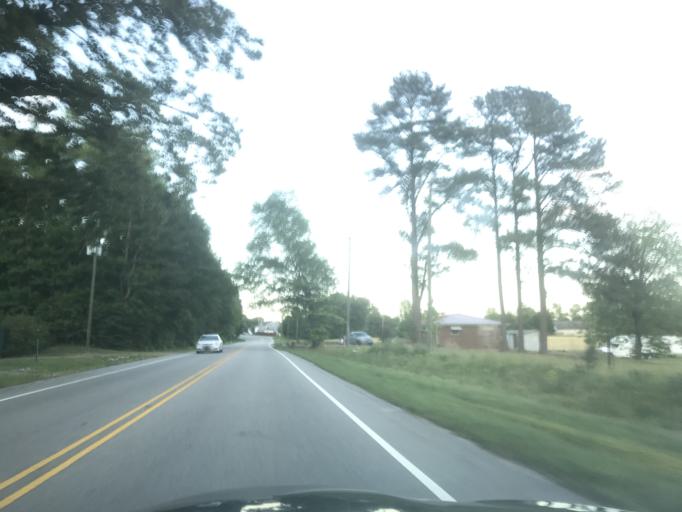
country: US
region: North Carolina
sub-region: Wake County
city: Wendell
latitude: 35.7759
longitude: -78.3820
